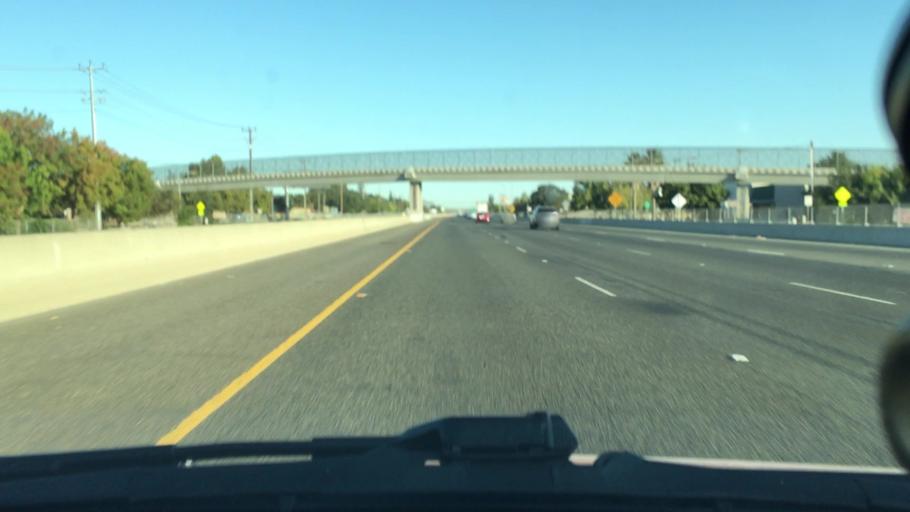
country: US
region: California
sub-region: Sacramento County
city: Elk Grove
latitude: 38.4115
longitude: -121.3898
